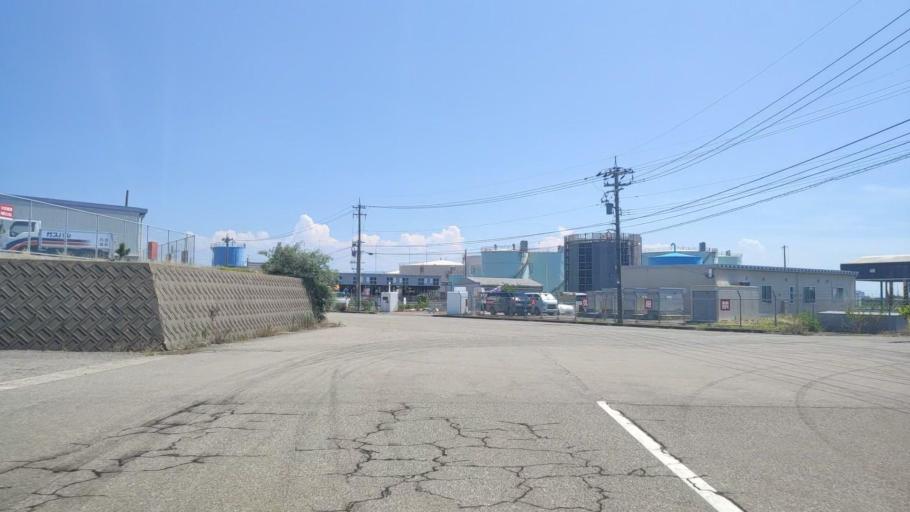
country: JP
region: Ishikawa
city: Kanazawa-shi
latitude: 36.6228
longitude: 136.6096
